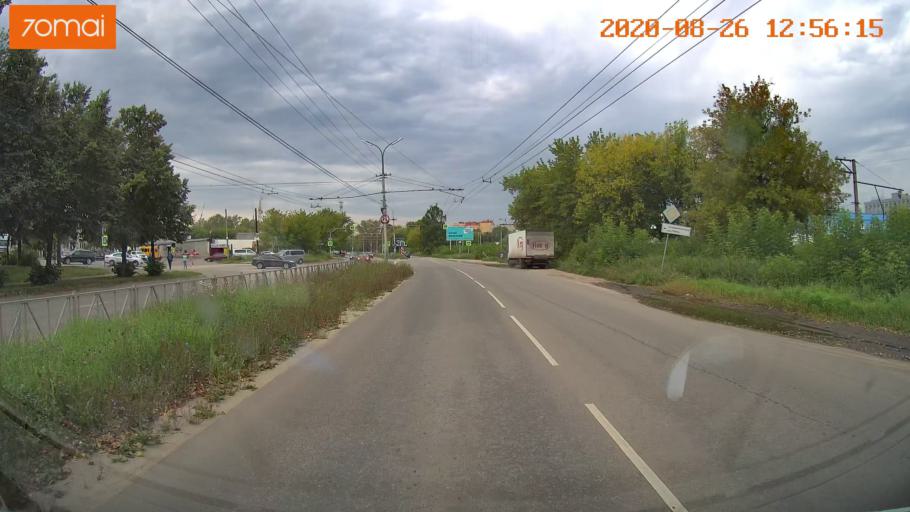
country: RU
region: Rjazan
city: Ryazan'
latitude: 54.6129
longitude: 39.7519
